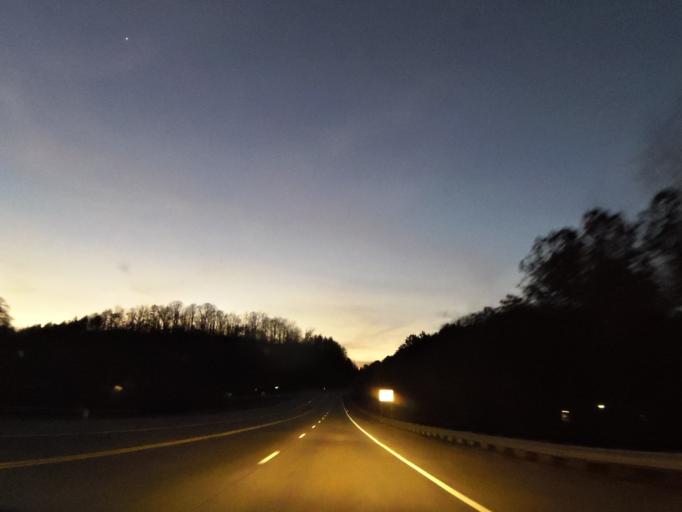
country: US
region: Georgia
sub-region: Whitfield County
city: Dalton
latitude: 34.7969
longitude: -84.9670
